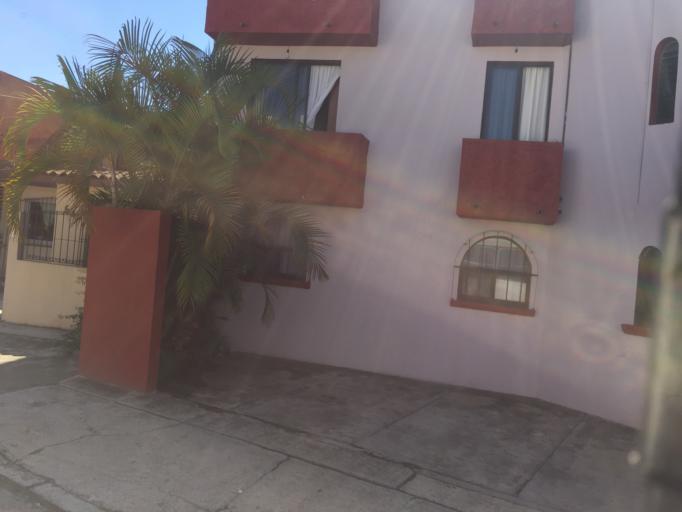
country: MX
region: Veracruz
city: El Castillo
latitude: 19.5323
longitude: -96.8873
